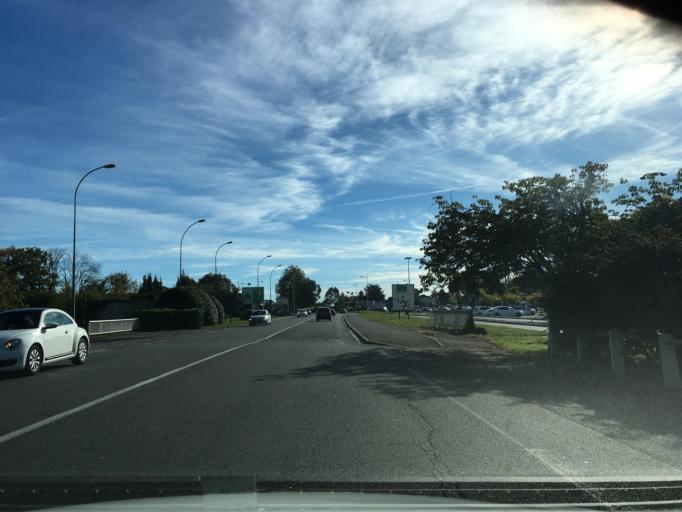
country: FR
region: Aquitaine
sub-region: Departement des Pyrenees-Atlantiques
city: Idron
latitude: 43.3060
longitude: -0.3315
